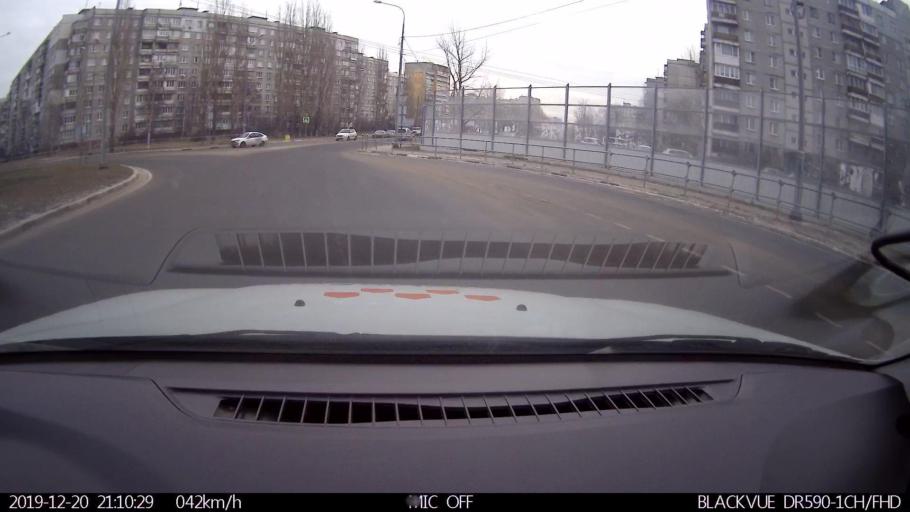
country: RU
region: Nizjnij Novgorod
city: Nizhniy Novgorod
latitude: 56.3454
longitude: 43.9234
